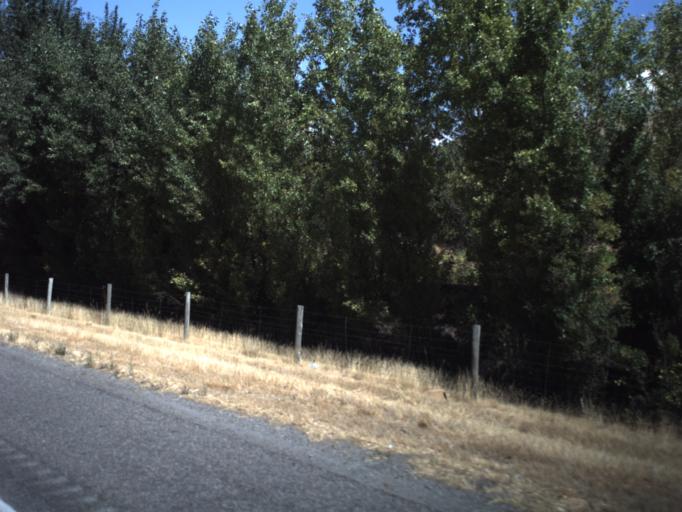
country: US
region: Utah
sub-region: Cache County
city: Richmond
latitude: 41.9549
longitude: -111.8130
